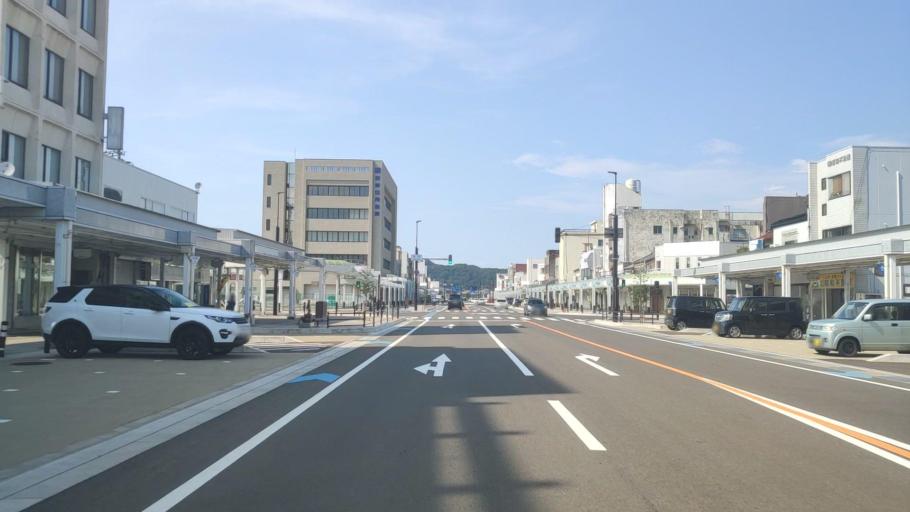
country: JP
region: Fukui
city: Tsuruga
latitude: 35.6506
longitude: 136.0726
